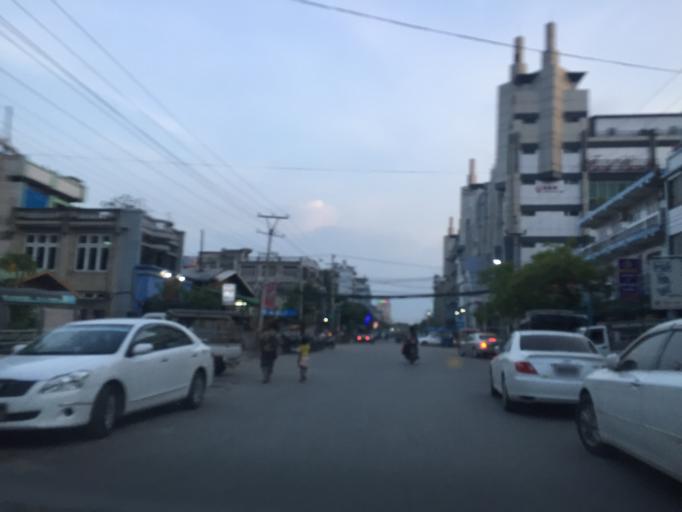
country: MM
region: Mandalay
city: Mandalay
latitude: 21.9727
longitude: 96.0883
